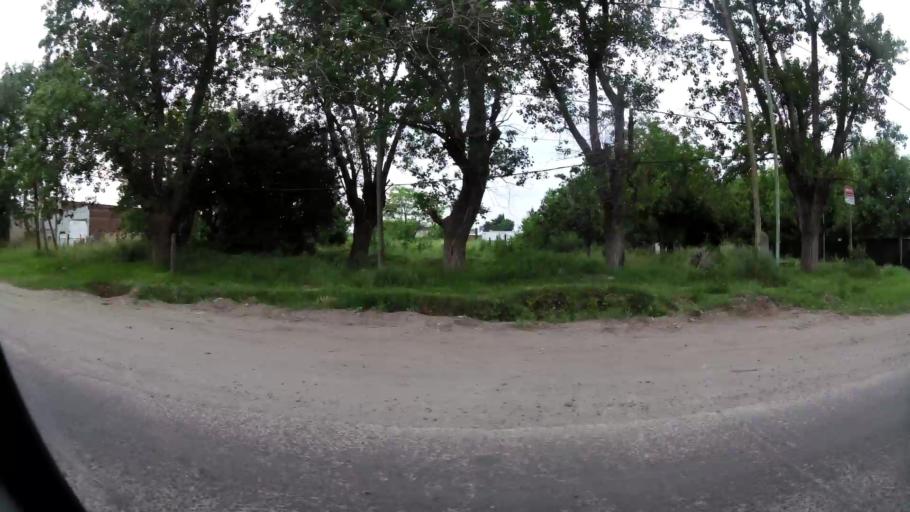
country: AR
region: Buenos Aires
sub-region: Partido de La Plata
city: La Plata
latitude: -34.9169
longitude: -58.0116
